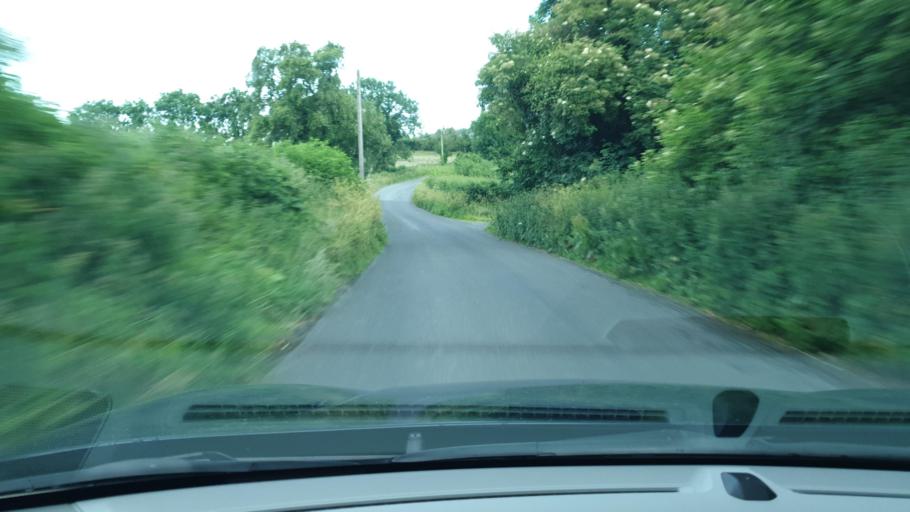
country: IE
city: Kentstown
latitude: 53.5921
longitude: -6.4863
